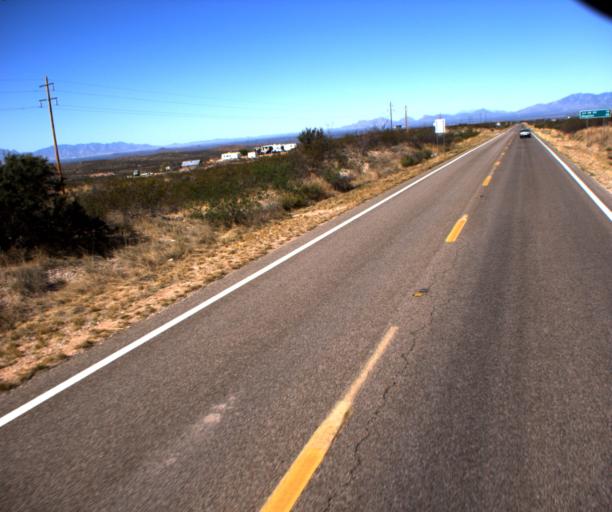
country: US
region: Arizona
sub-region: Cochise County
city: Tombstone
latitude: 31.7482
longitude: -110.1017
